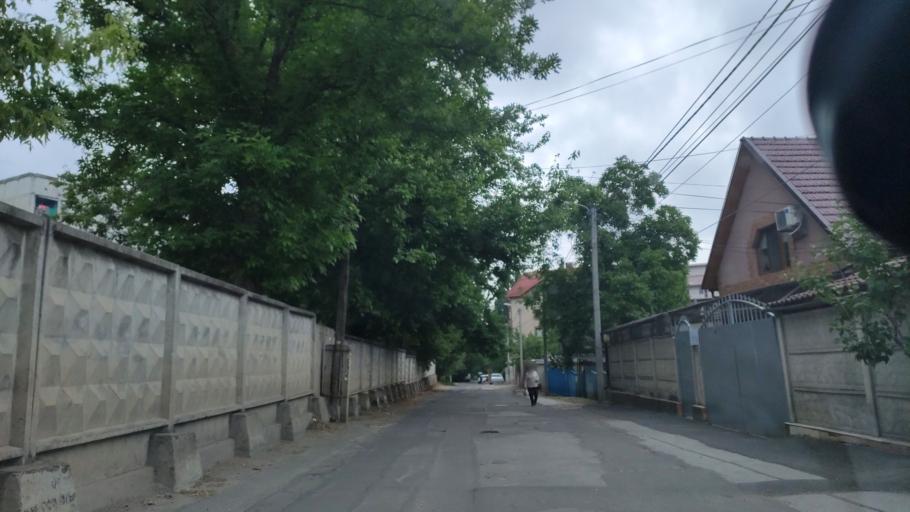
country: MD
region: Chisinau
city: Chisinau
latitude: 46.9858
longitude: 28.8714
